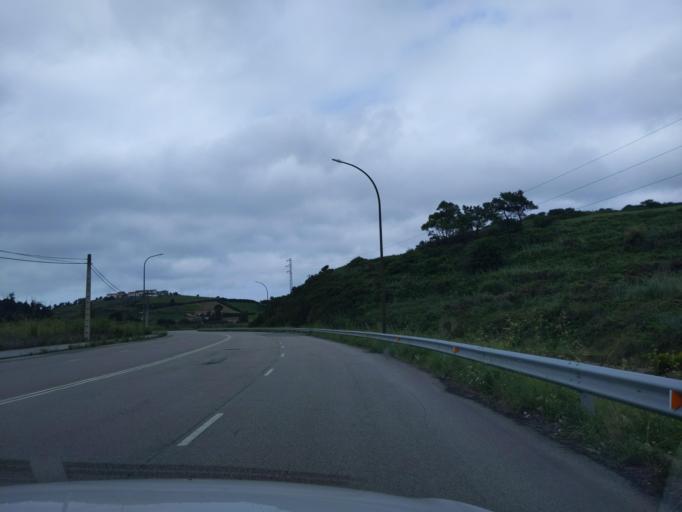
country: ES
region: Asturias
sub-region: Province of Asturias
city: Aviles
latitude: 43.5919
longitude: -5.9150
